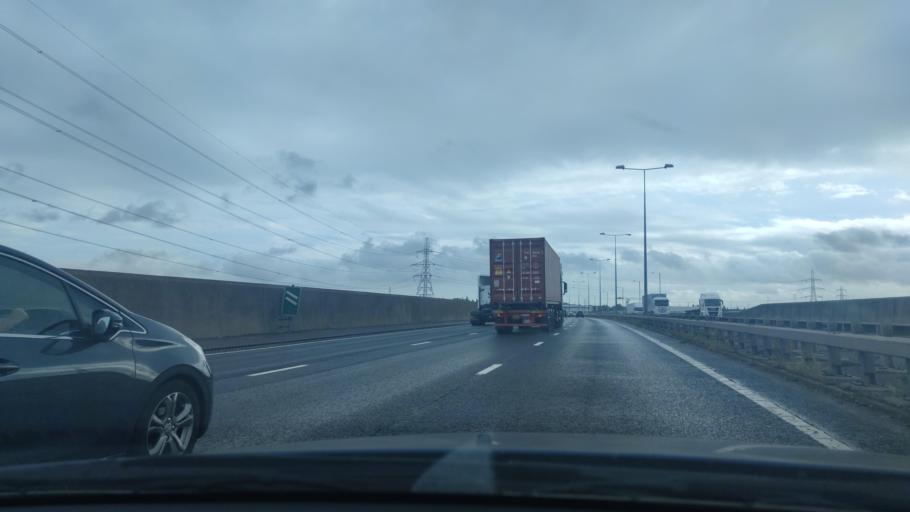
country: GB
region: England
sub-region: Essex
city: Purfleet
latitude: 51.5015
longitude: 0.2165
